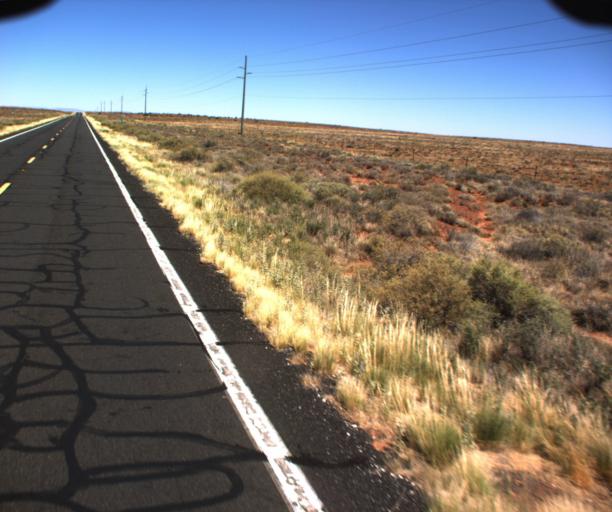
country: US
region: Arizona
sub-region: Coconino County
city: LeChee
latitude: 34.8775
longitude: -110.8901
